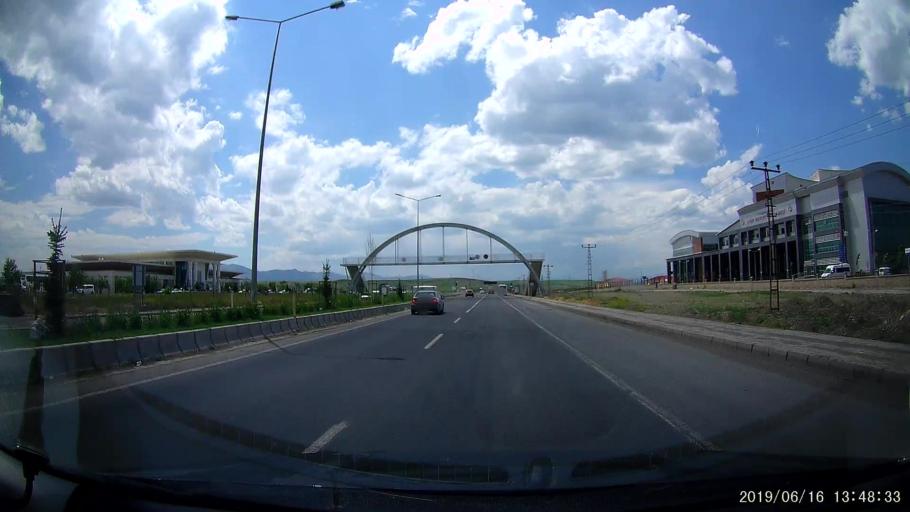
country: TR
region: Agri
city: Agri
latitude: 39.7145
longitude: 43.0048
